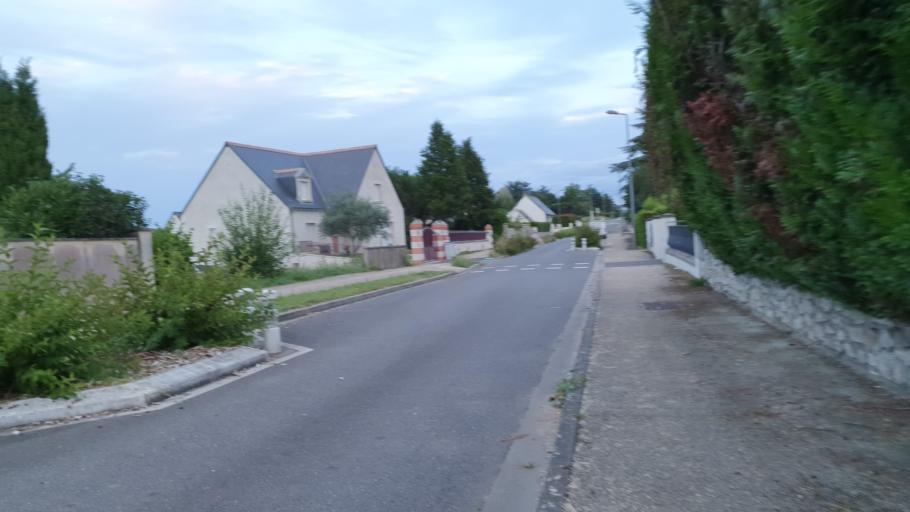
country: FR
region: Centre
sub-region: Departement d'Indre-et-Loire
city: Larcay
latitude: 47.3607
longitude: 0.7761
